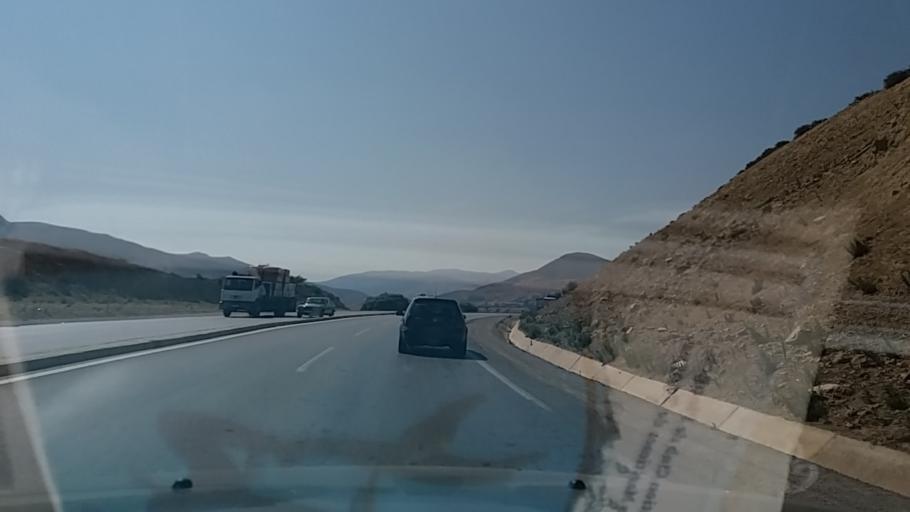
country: MA
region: Tanger-Tetouan
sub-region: Tetouan
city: Saddina
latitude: 35.5580
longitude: -5.4483
